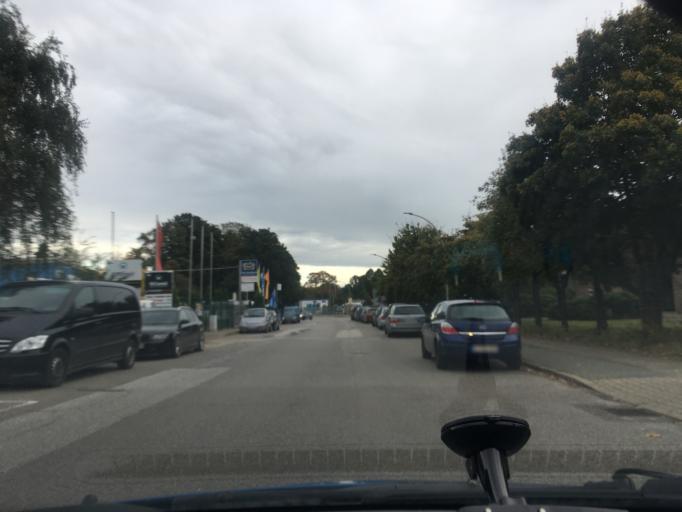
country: DE
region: Schleswig-Holstein
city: Geesthacht
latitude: 53.4346
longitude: 10.3438
